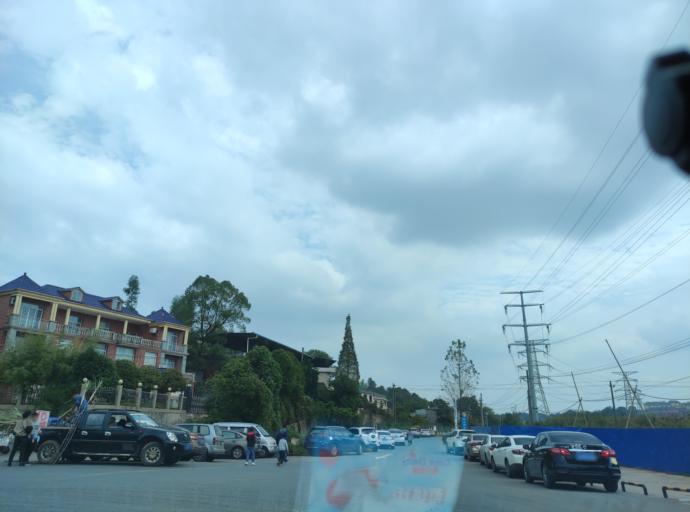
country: CN
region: Jiangxi Sheng
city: Pingxiang
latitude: 27.6627
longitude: 113.9116
